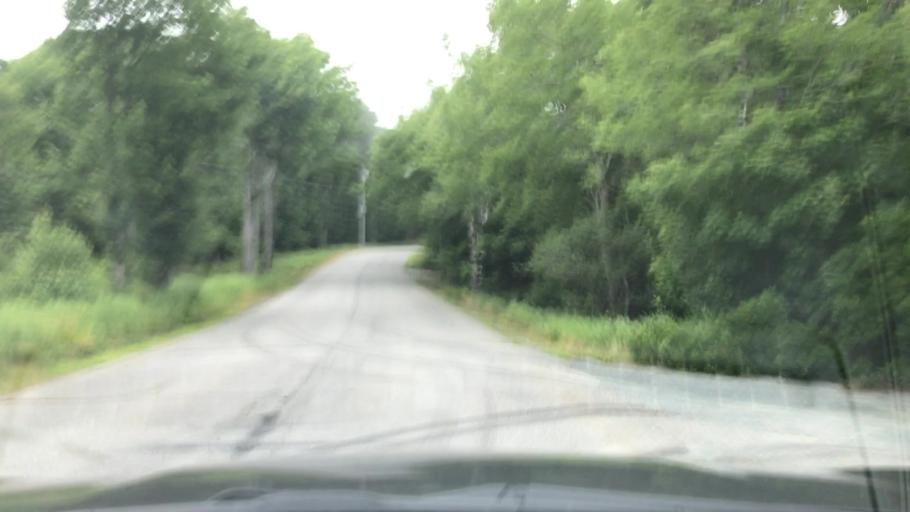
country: US
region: Maine
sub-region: Hancock County
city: Bar Harbor
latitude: 44.3435
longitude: -68.1793
